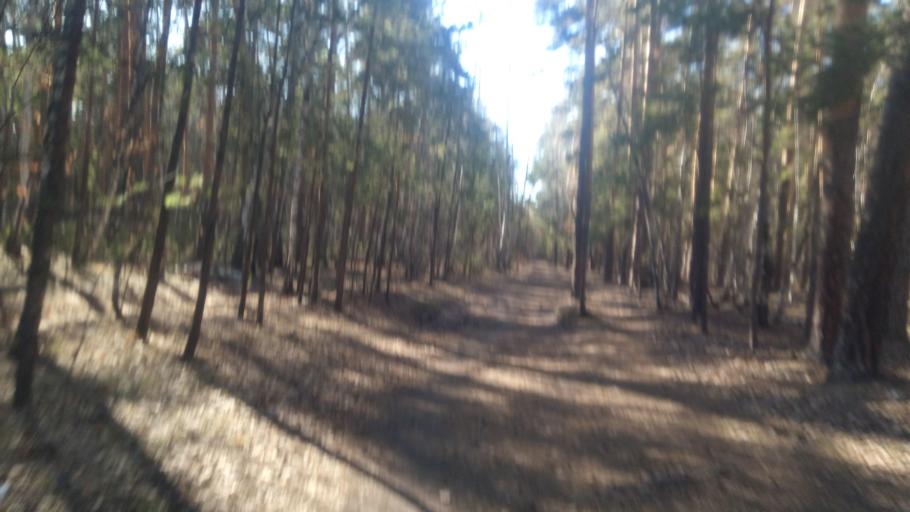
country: RU
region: Chelyabinsk
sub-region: Gorod Chelyabinsk
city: Chelyabinsk
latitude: 55.1571
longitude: 61.3467
